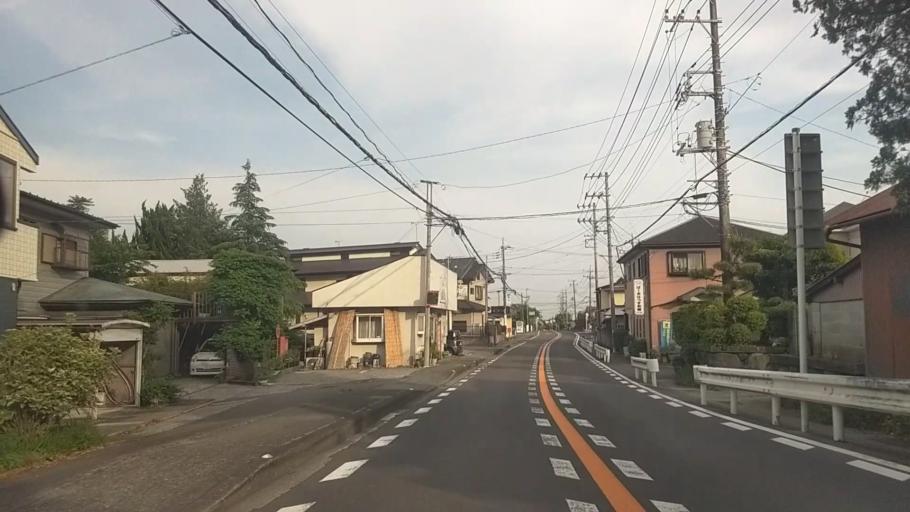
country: JP
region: Kanagawa
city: Odawara
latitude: 35.3552
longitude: 139.0905
